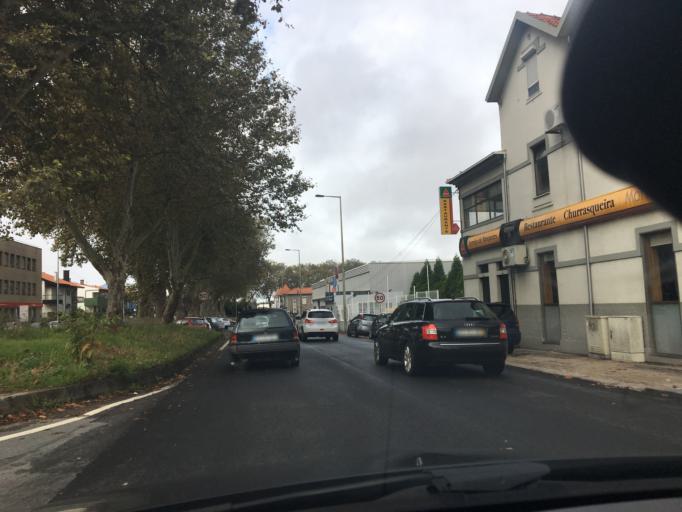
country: PT
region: Porto
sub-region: Matosinhos
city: Senhora da Hora
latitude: 41.1796
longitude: -8.6296
